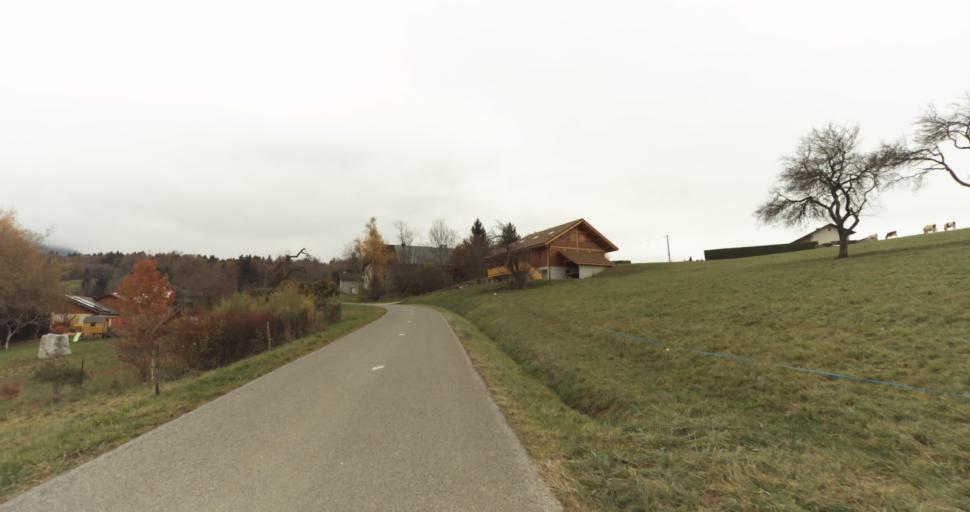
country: FR
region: Rhone-Alpes
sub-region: Departement de la Haute-Savoie
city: Groisy
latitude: 45.9917
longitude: 6.2031
